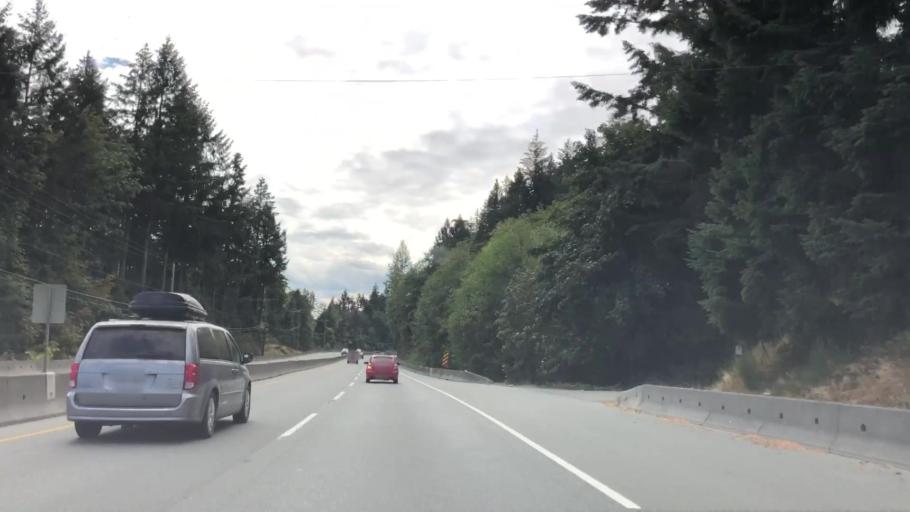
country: CA
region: British Columbia
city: North Cowichan
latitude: 48.8591
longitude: -123.7168
